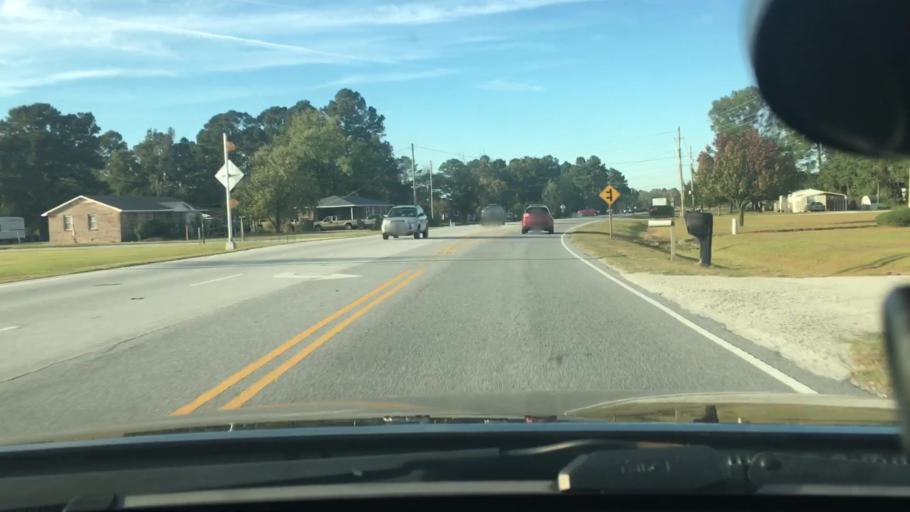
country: US
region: North Carolina
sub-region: Pitt County
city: Windsor
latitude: 35.5139
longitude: -77.3190
